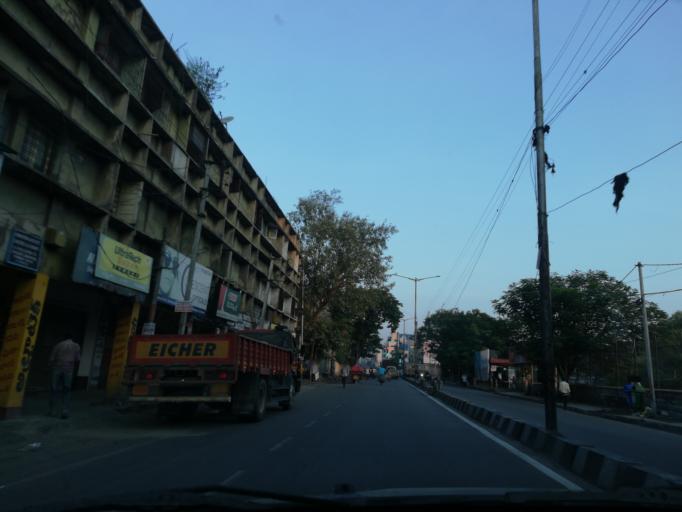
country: IN
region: Telangana
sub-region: Rangareddi
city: Gaddi Annaram
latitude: 17.3956
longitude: 78.4974
